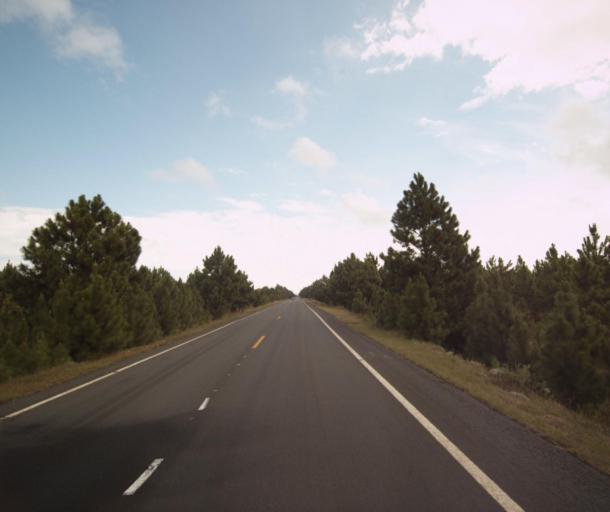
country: BR
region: Rio Grande do Sul
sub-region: Tapes
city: Tapes
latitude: -31.4261
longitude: -51.1844
